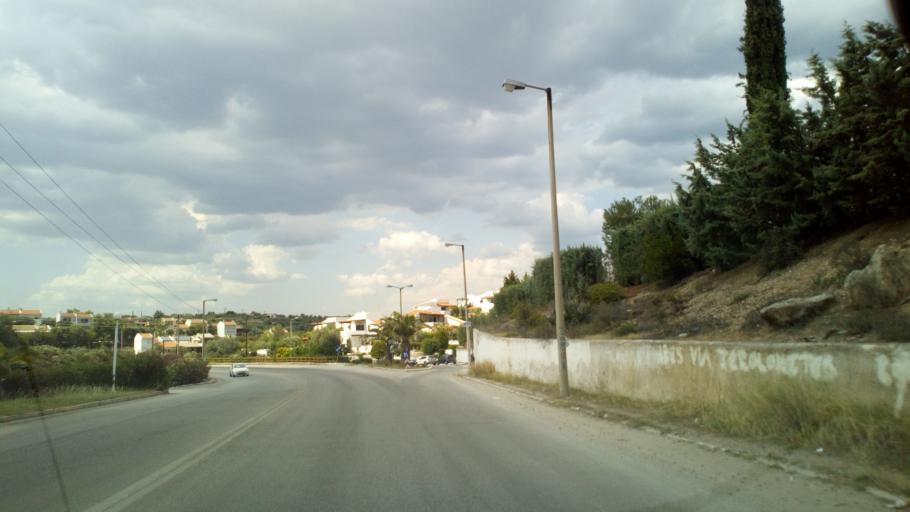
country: GR
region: Central Macedonia
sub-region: Nomos Chalkidikis
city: Ormylia
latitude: 40.2631
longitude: 23.4720
